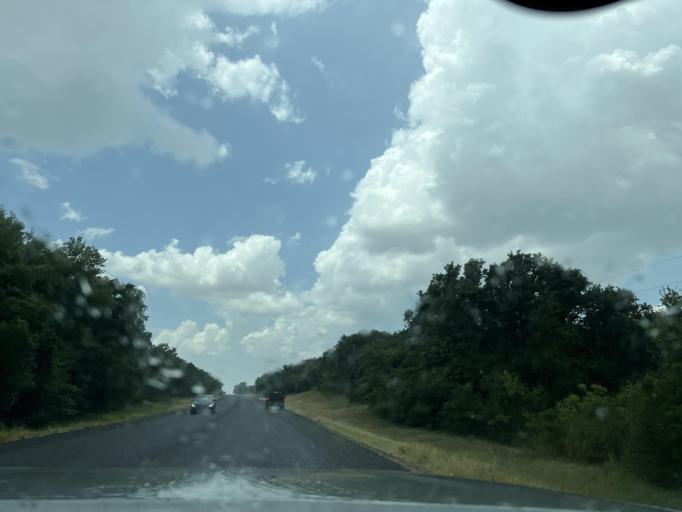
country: US
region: Texas
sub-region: Wise County
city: Boyd
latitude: 33.1194
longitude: -97.6537
